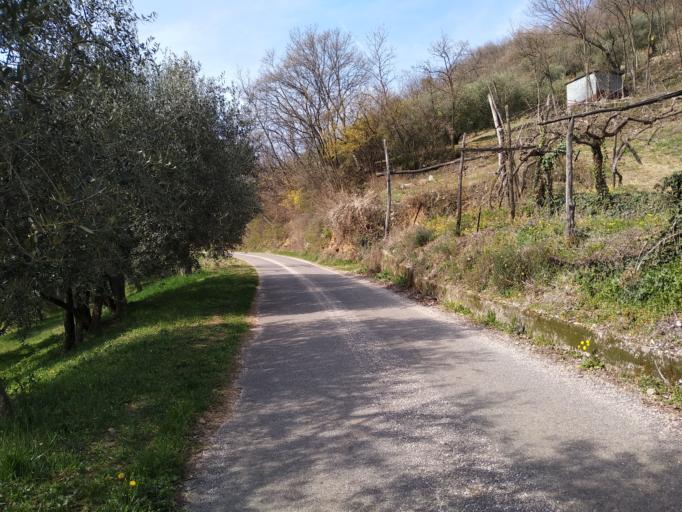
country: IT
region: Veneto
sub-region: Provincia di Vicenza
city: Barbarano Vicentino
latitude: 45.4140
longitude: 11.5389
